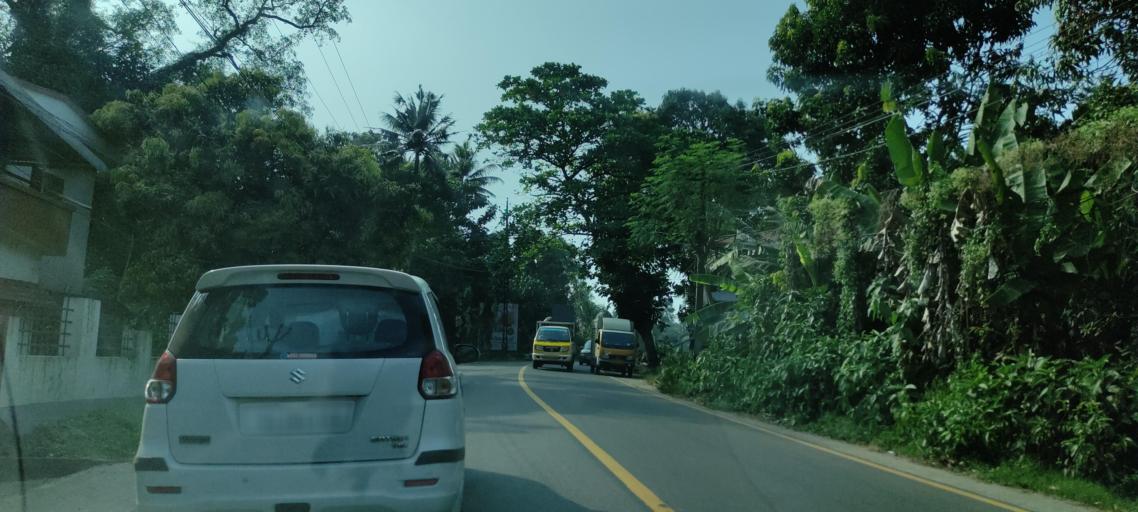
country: IN
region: Kerala
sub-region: Pattanamtitta
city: Tiruvalla
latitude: 9.3676
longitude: 76.5321
